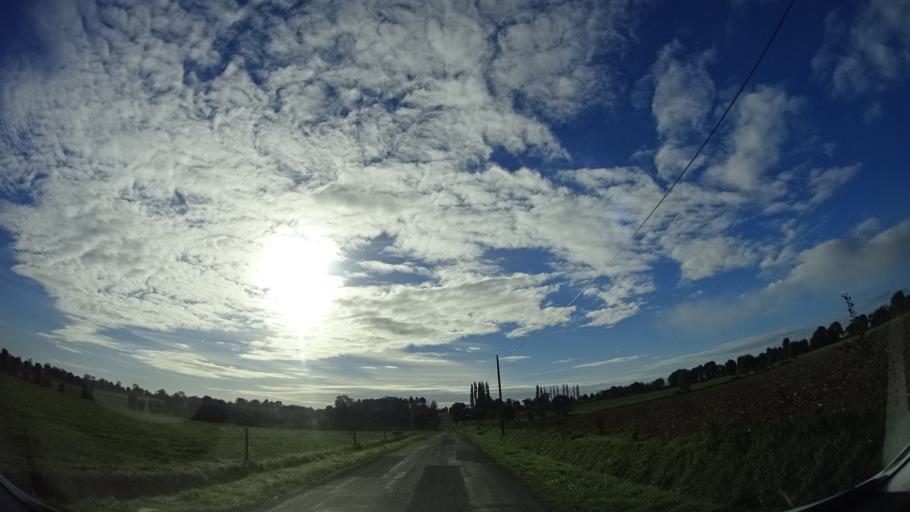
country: FR
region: Brittany
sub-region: Departement d'Ille-et-Vilaine
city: Geveze
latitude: 48.1961
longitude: -1.8196
